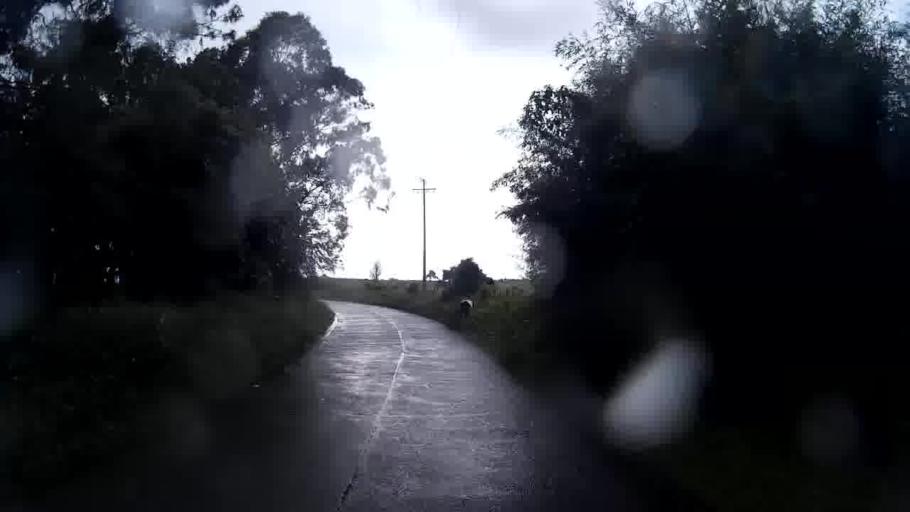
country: CO
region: Quindio
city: Filandia
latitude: 4.6879
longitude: -75.6182
